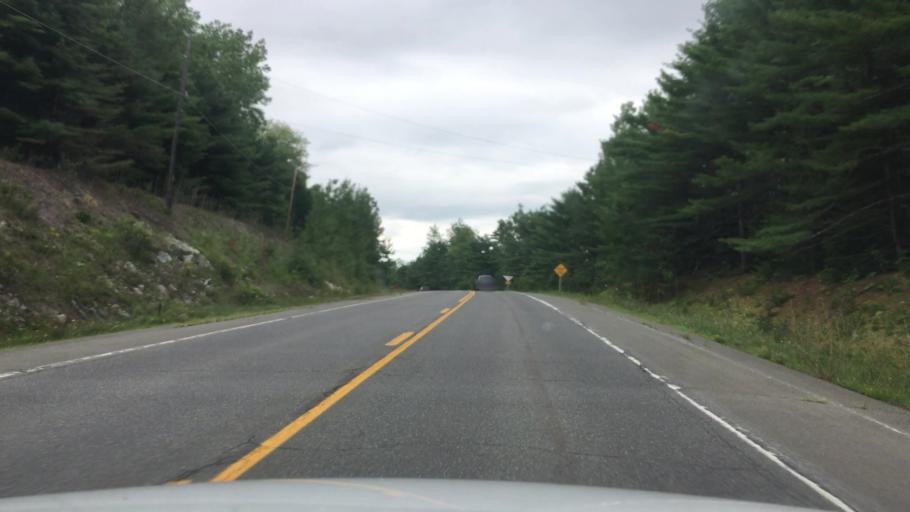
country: US
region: Maine
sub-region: Penobscot County
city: Bradley
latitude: 44.8245
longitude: -68.4018
